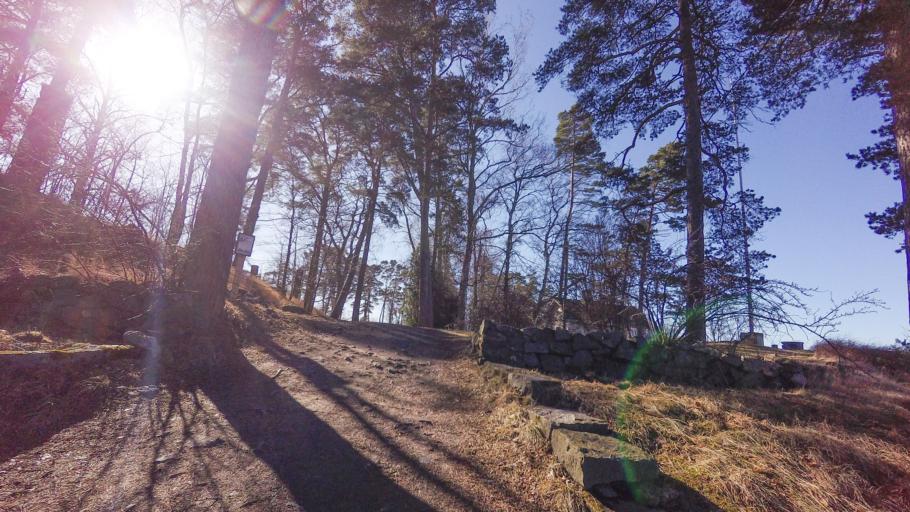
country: FI
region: Uusimaa
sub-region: Helsinki
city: Vantaa
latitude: 60.1560
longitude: 25.0821
